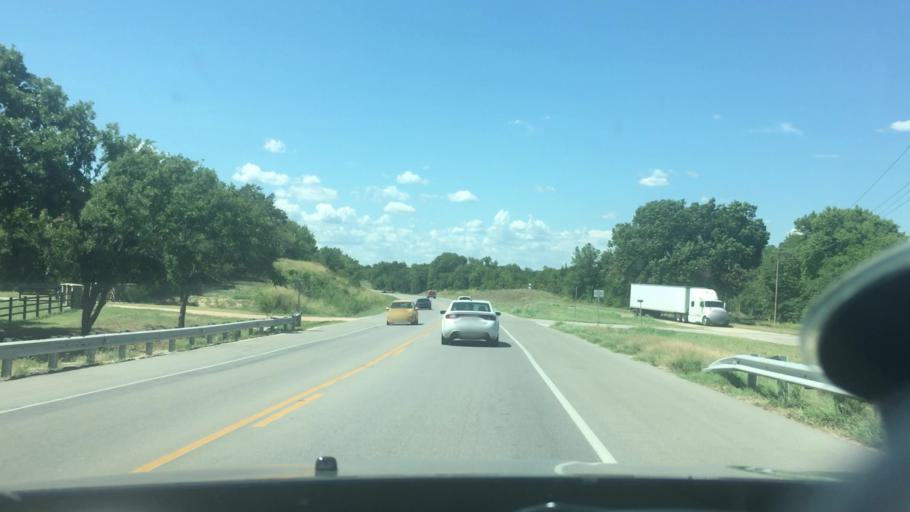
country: US
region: Oklahoma
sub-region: Marshall County
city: Kingston
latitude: 34.0272
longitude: -96.7266
